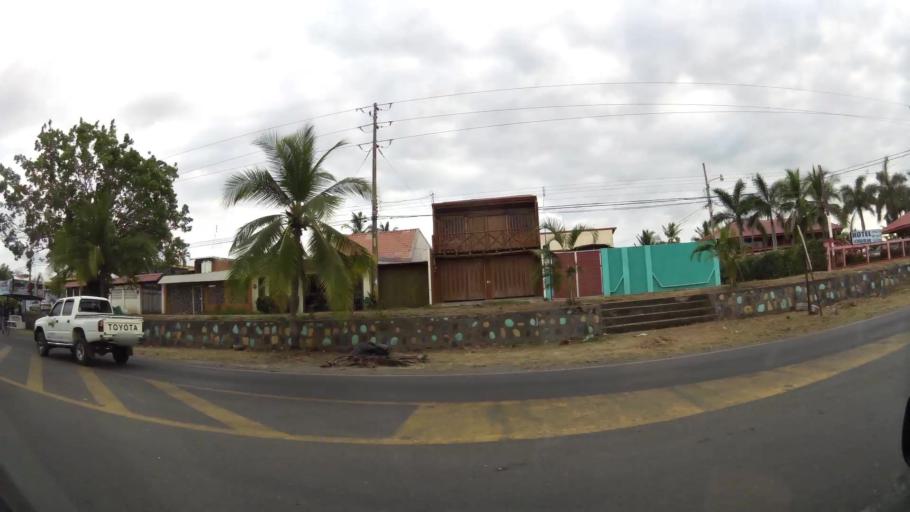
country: CR
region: Puntarenas
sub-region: Canton Central de Puntarenas
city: Puntarenas
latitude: 9.9808
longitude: -84.8129
